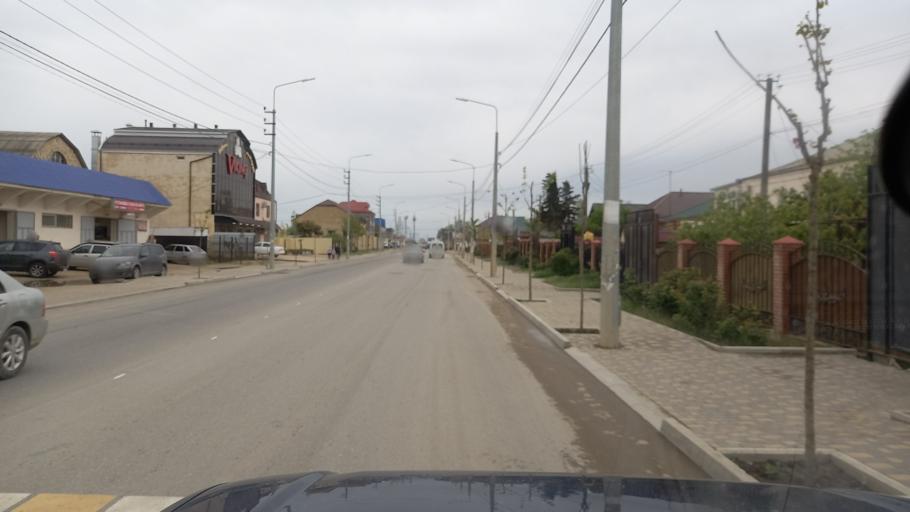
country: RU
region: Dagestan
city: Derbent
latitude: 42.0816
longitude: 48.2947
